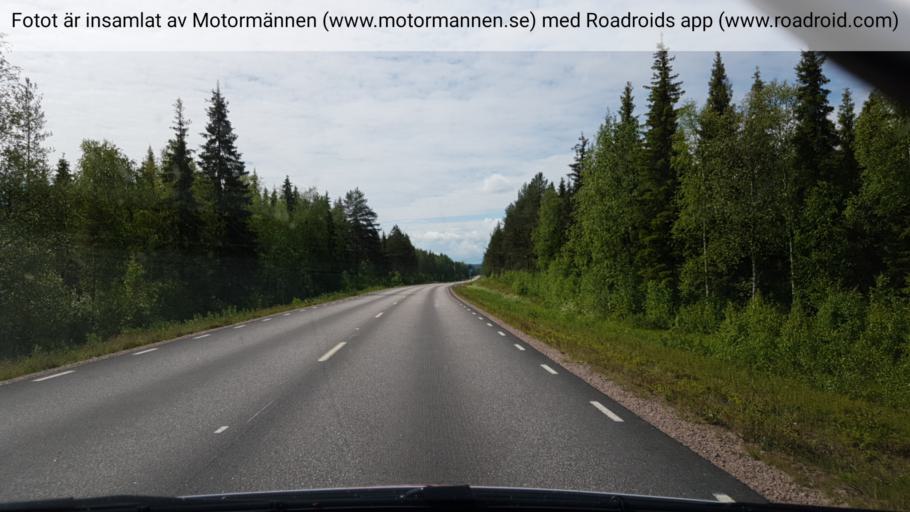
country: SE
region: Norrbotten
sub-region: Overtornea Kommun
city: OEvertornea
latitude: 66.4818
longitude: 23.6980
